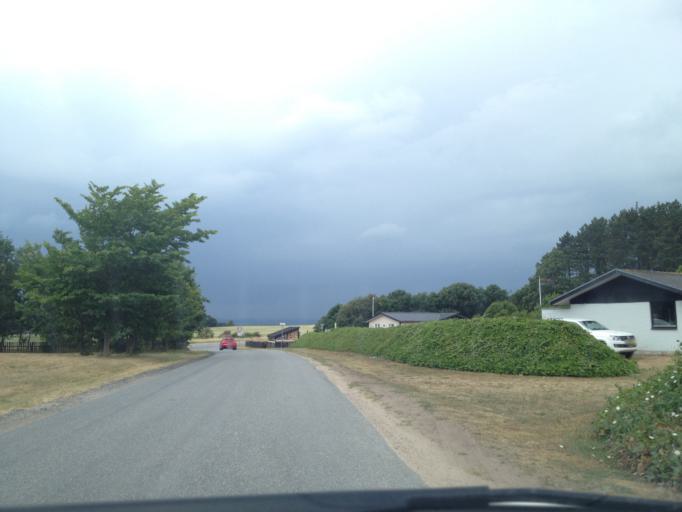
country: DK
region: Central Jutland
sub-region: Syddjurs Kommune
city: Ebeltoft
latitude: 56.1700
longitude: 10.6715
